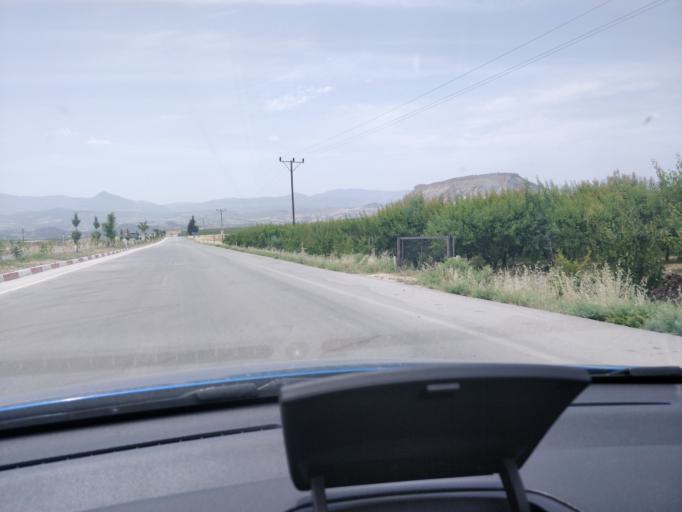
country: TR
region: Mersin
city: Mut
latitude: 36.6048
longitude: 33.4365
